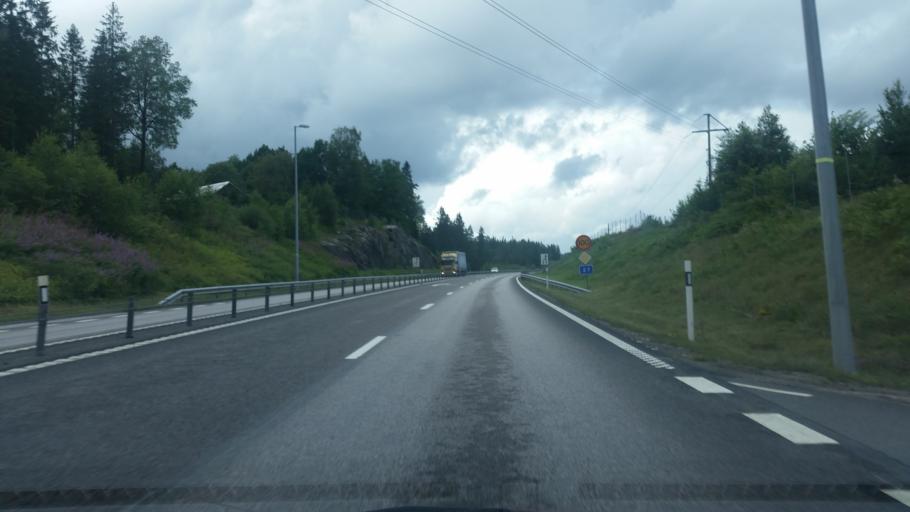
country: SE
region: Vaestra Goetaland
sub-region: Boras Kommun
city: Ganghester
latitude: 57.6587
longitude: 13.0436
